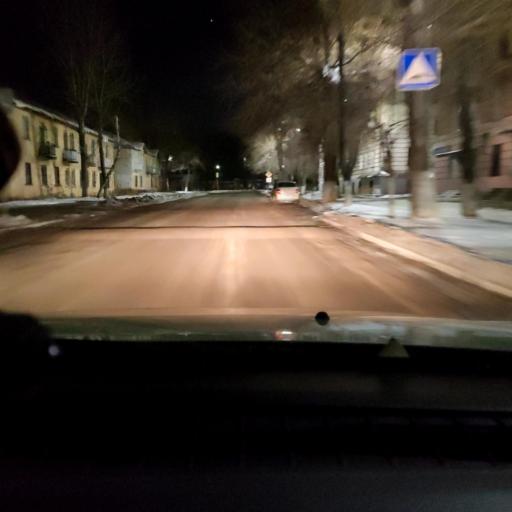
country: RU
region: Samara
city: Novokuybyshevsk
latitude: 53.0998
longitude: 49.9524
